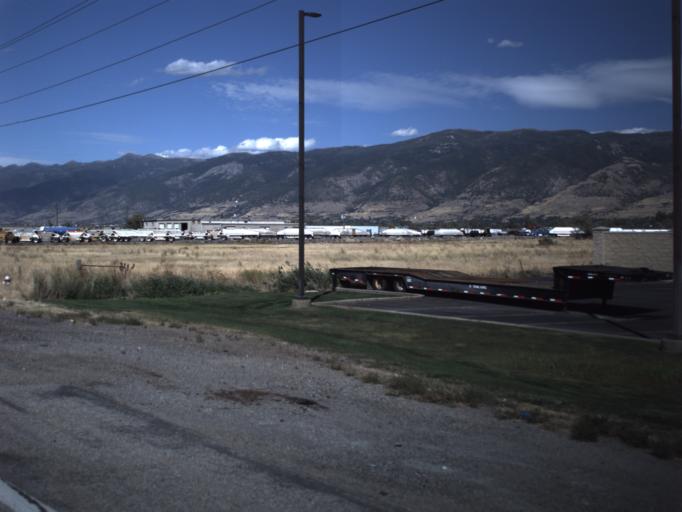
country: US
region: Utah
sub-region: Davis County
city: West Bountiful
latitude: 40.8782
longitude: -111.9300
